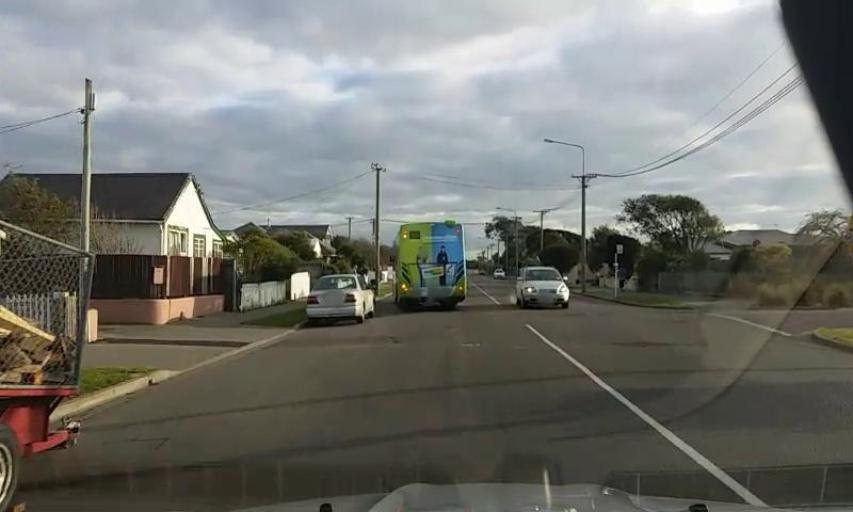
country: NZ
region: Canterbury
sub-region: Christchurch City
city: Christchurch
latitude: -43.5217
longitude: 172.7319
